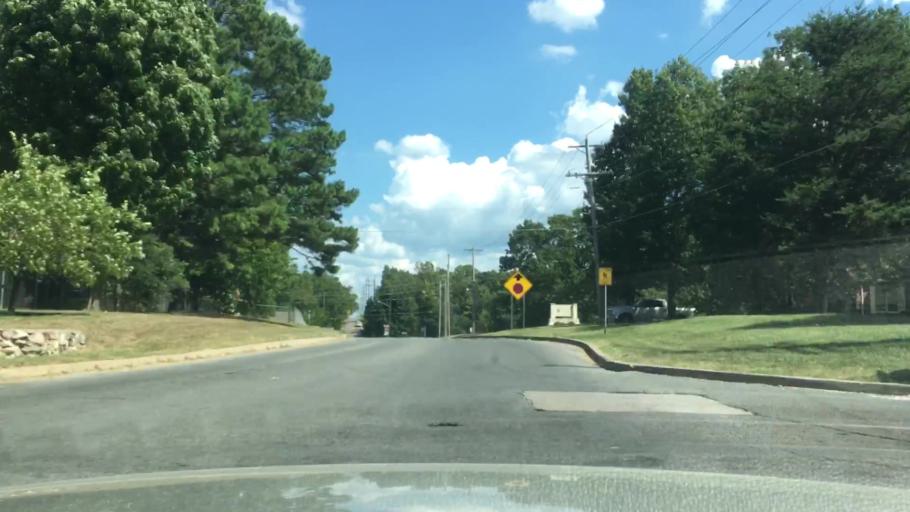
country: US
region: Oklahoma
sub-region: Cherokee County
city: Tahlequah
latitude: 35.9226
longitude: -94.9578
